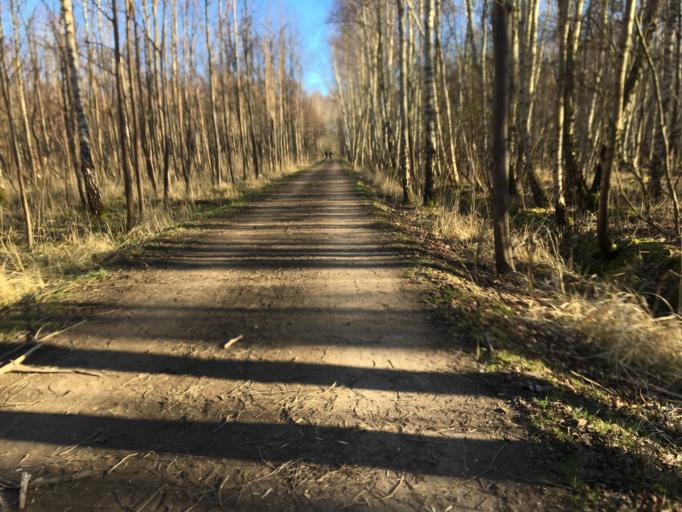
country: DK
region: Capital Region
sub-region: Tarnby Kommune
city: Tarnby
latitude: 55.5947
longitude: 12.5543
